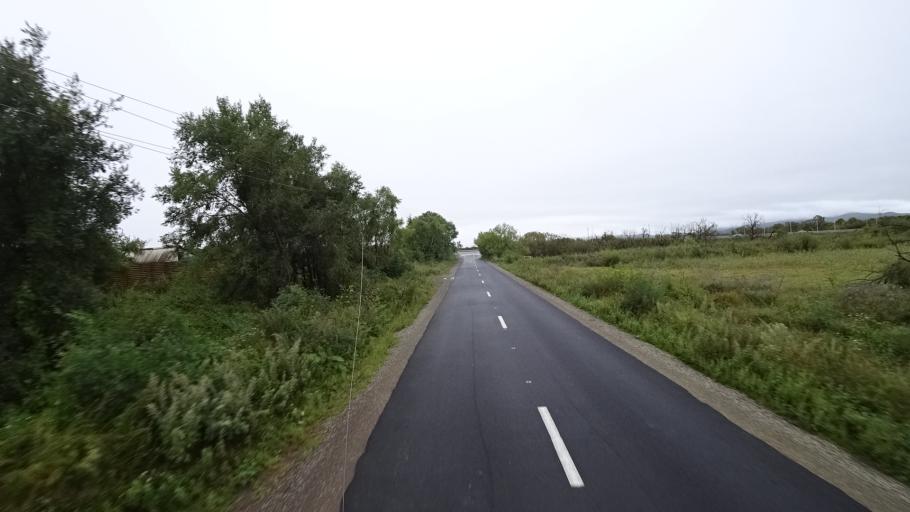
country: RU
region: Primorskiy
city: Monastyrishche
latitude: 44.2000
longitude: 132.4460
